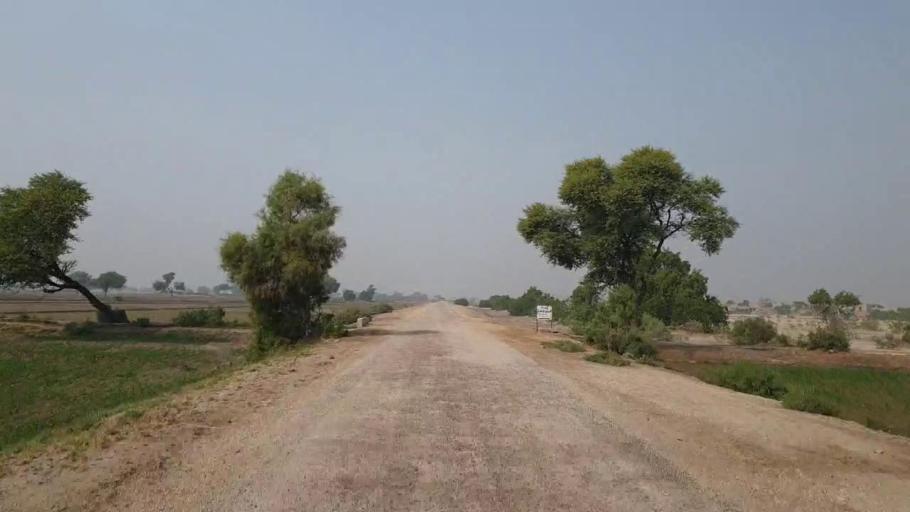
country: PK
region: Sindh
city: Bhan
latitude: 26.4992
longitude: 67.6960
